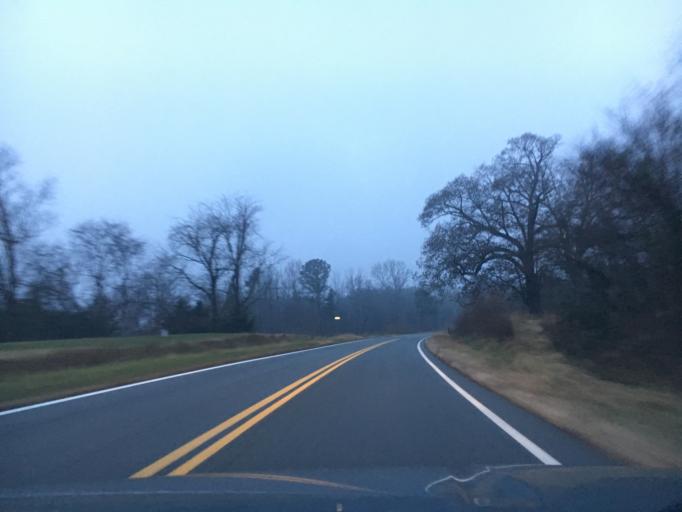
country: US
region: Virginia
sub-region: Halifax County
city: Mountain Road
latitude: 36.6837
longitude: -78.9947
